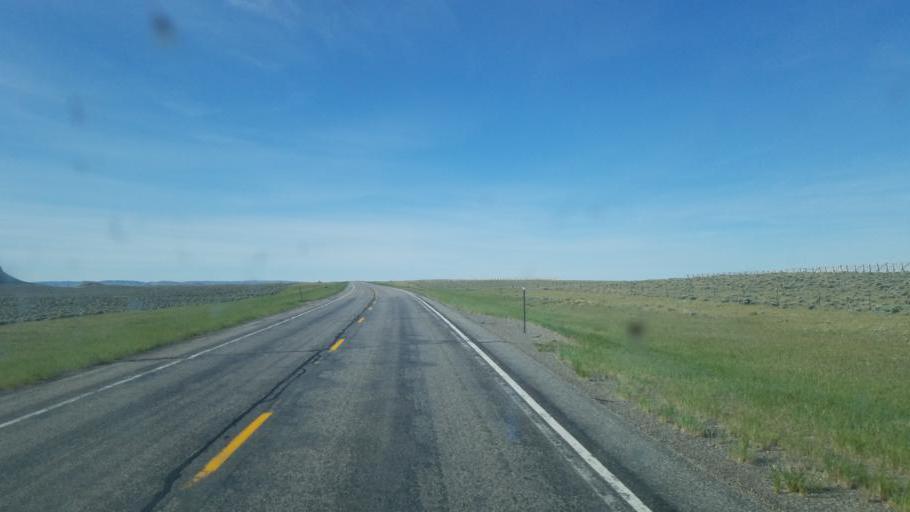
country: US
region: Wyoming
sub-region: Fremont County
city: Riverton
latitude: 42.6452
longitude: -108.1935
